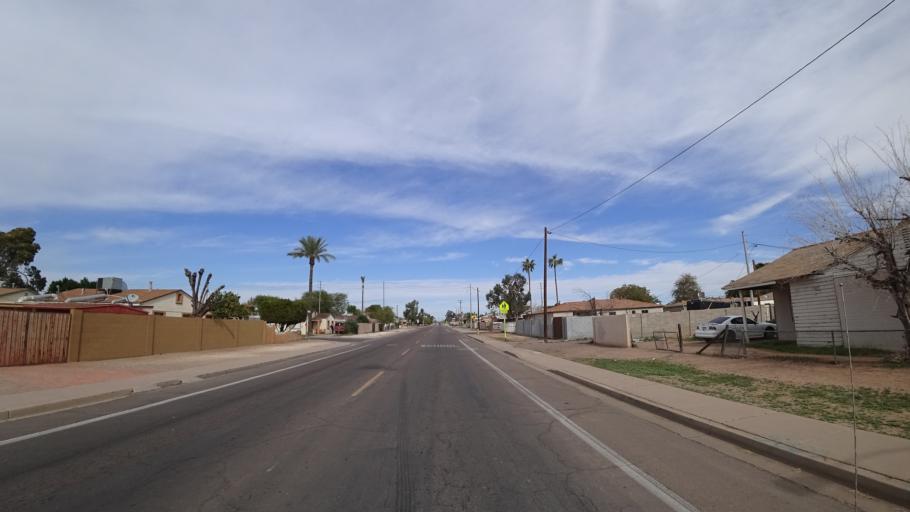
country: US
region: Arizona
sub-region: Maricopa County
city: Phoenix
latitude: 33.4573
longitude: -112.1259
